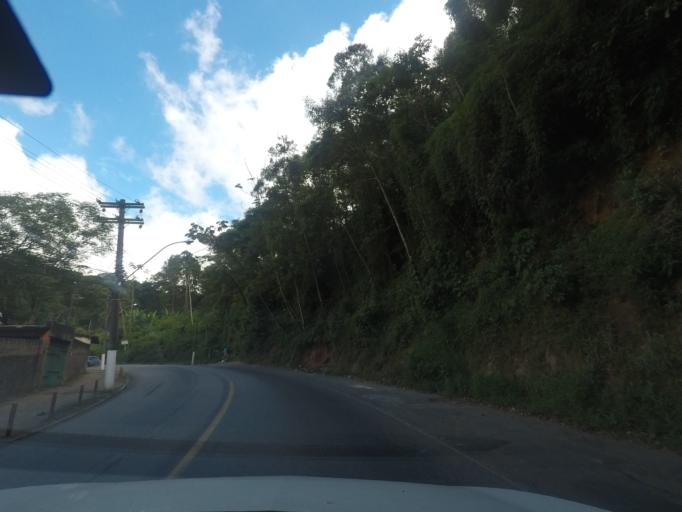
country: BR
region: Rio de Janeiro
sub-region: Teresopolis
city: Teresopolis
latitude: -22.3971
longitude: -42.9591
